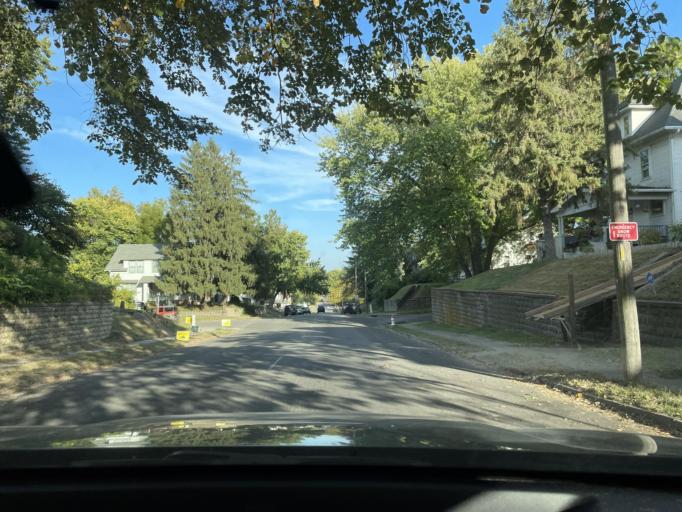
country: US
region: Missouri
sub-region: Buchanan County
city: Saint Joseph
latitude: 39.7683
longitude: -94.8291
